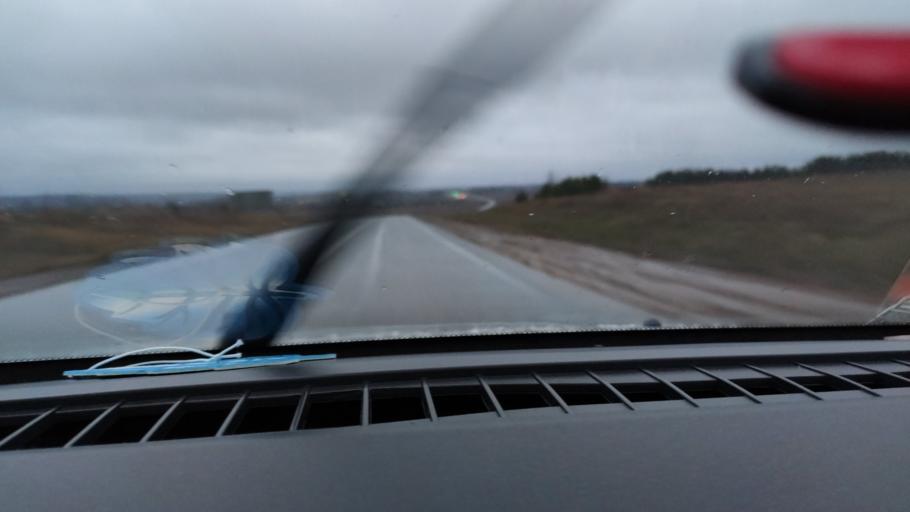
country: RU
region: Udmurtiya
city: Alnashi
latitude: 56.1927
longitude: 52.4560
